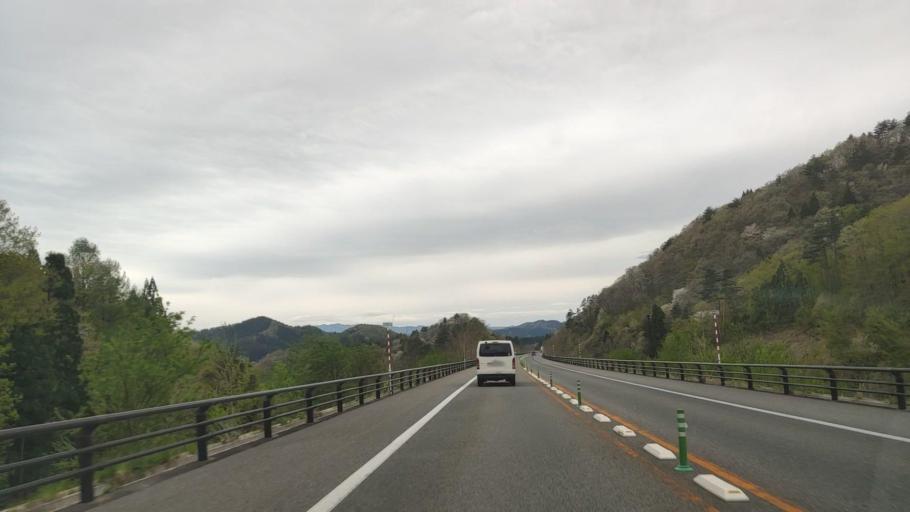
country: JP
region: Akita
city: Odate
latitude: 40.3221
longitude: 140.5968
